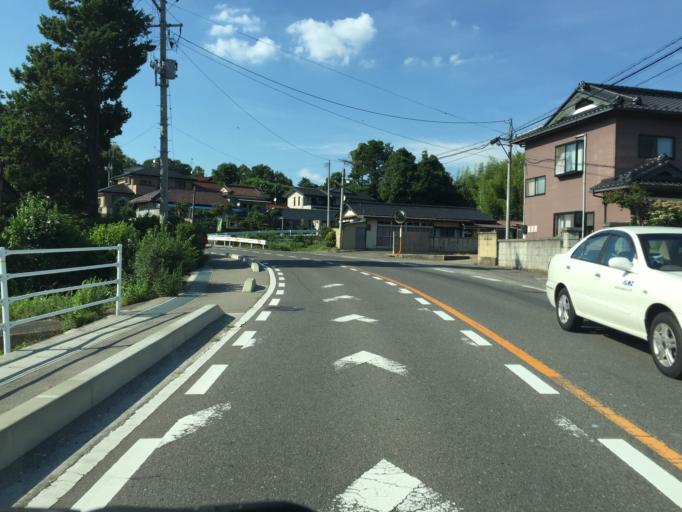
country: JP
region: Fukushima
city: Koriyama
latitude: 37.4295
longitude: 140.3927
